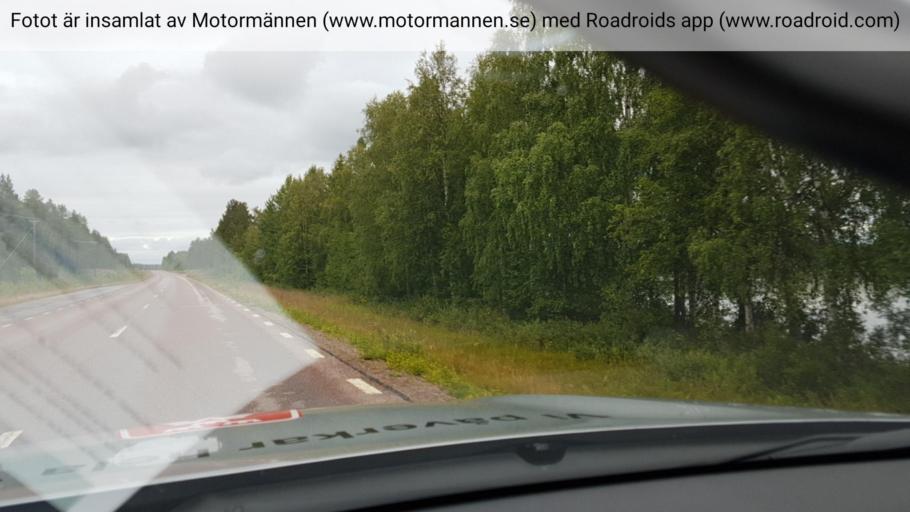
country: SE
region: Norrbotten
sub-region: Pajala Kommun
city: Pajala
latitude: 67.1181
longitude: 22.6049
